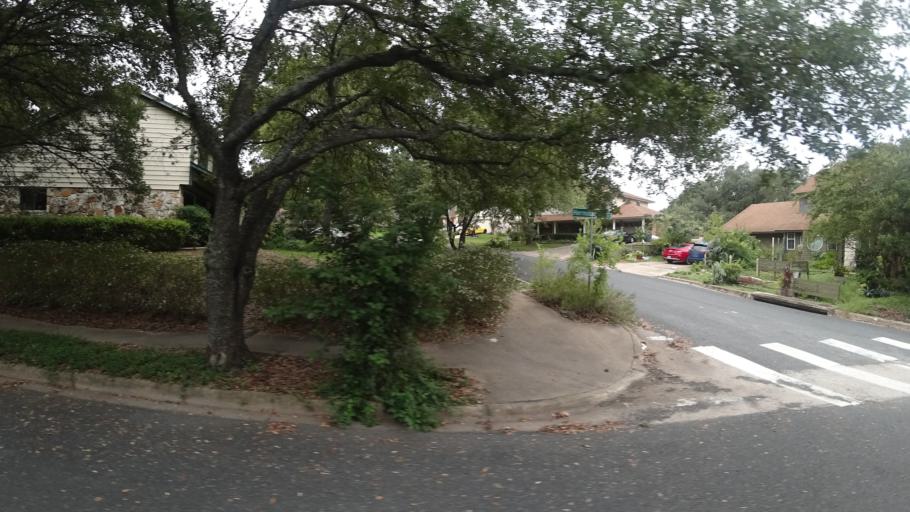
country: US
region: Texas
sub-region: Travis County
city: Austin
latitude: 30.3476
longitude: -97.6886
